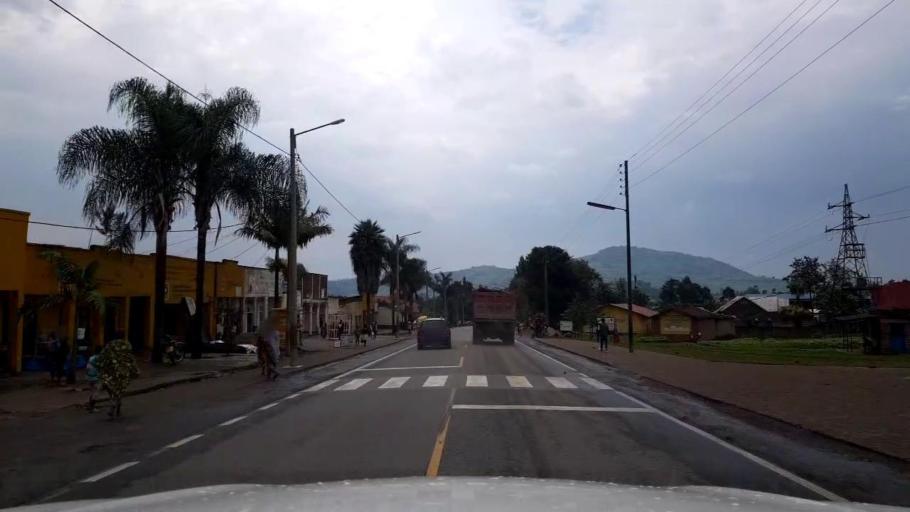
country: RW
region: Western Province
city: Gisenyi
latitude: -1.6937
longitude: 29.3064
